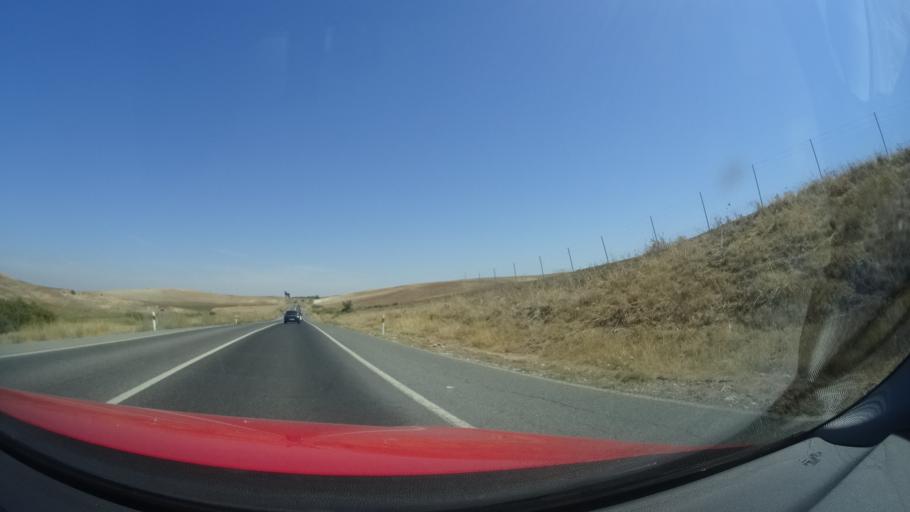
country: ES
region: Andalusia
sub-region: Provincia de Sevilla
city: Las Cabezas de San Juan
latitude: 36.9617
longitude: -5.8864
